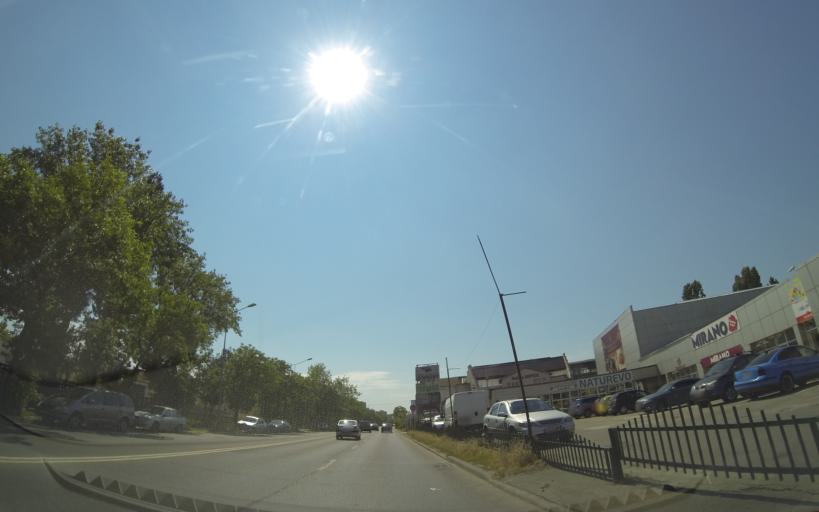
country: RO
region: Bucuresti
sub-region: Municipiul Bucuresti
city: Bucuresti
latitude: 44.4214
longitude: 26.0710
